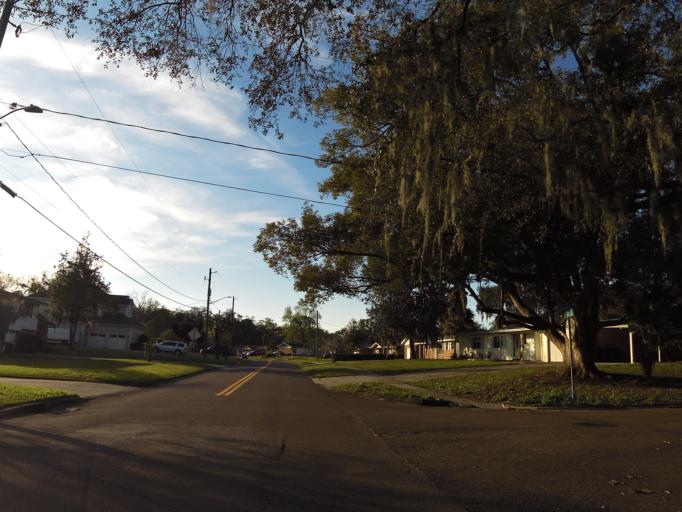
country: US
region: Florida
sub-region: Duval County
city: Jacksonville
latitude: 30.4390
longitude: -81.6349
